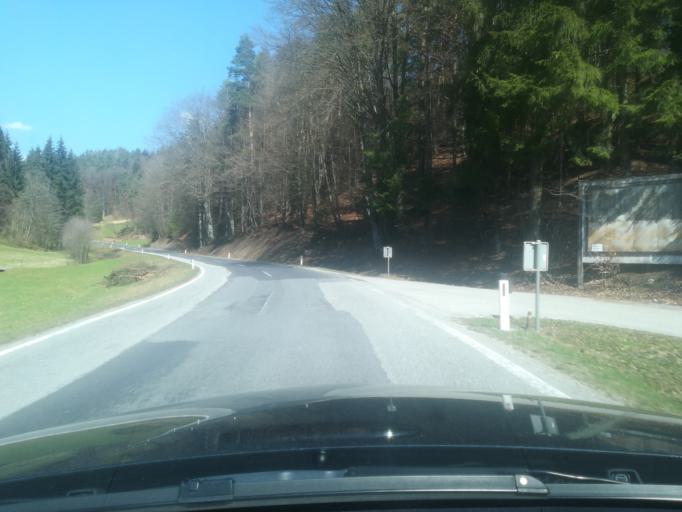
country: AT
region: Upper Austria
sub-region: Politischer Bezirk Perg
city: Bad Kreuzen
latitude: 48.4001
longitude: 14.7336
